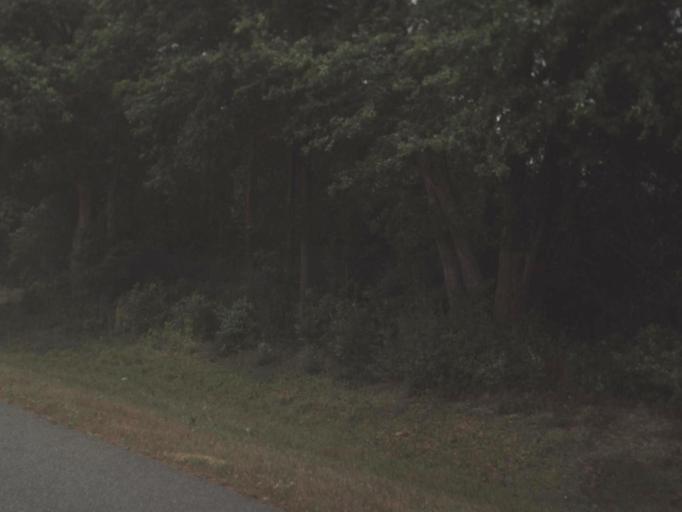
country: US
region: Florida
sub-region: Santa Rosa County
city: Point Baker
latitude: 30.8056
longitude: -87.0970
